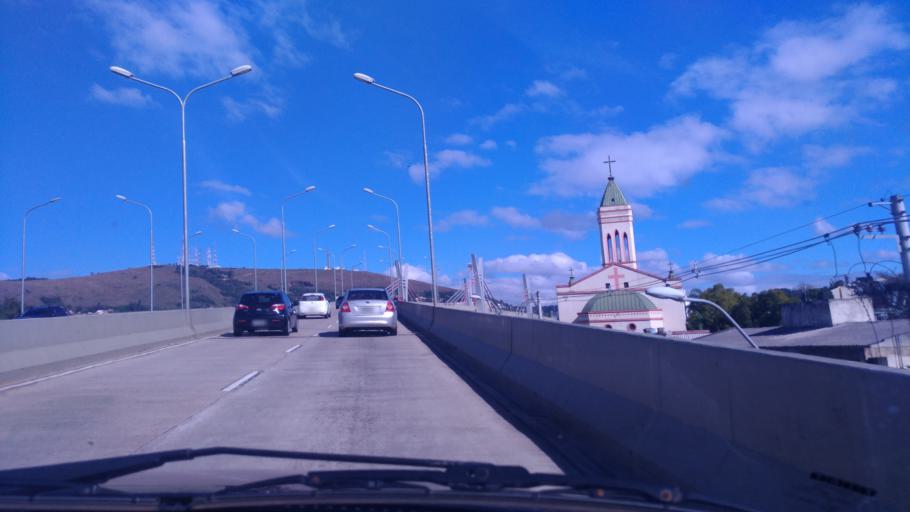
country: BR
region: Rio Grande do Sul
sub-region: Porto Alegre
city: Porto Alegre
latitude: -30.0620
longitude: -51.1851
